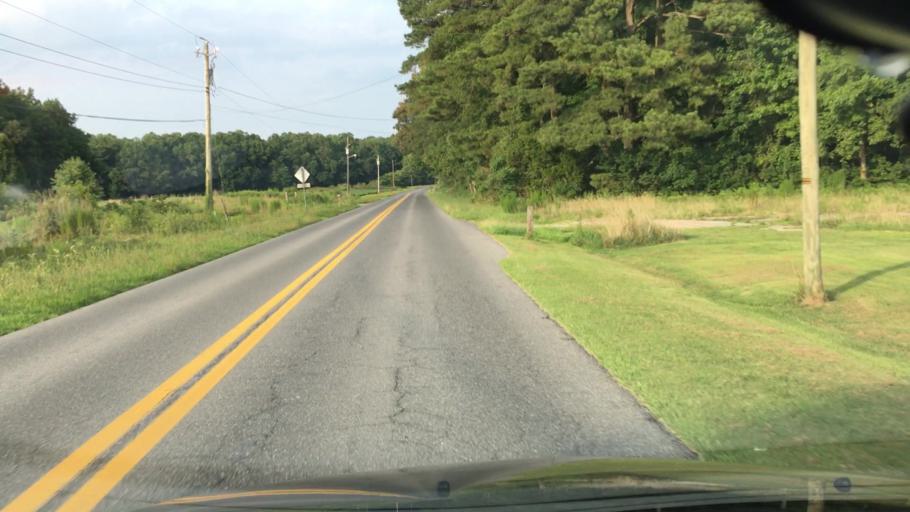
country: US
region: Delaware
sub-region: Sussex County
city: Selbyville
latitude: 38.4664
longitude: -75.1530
